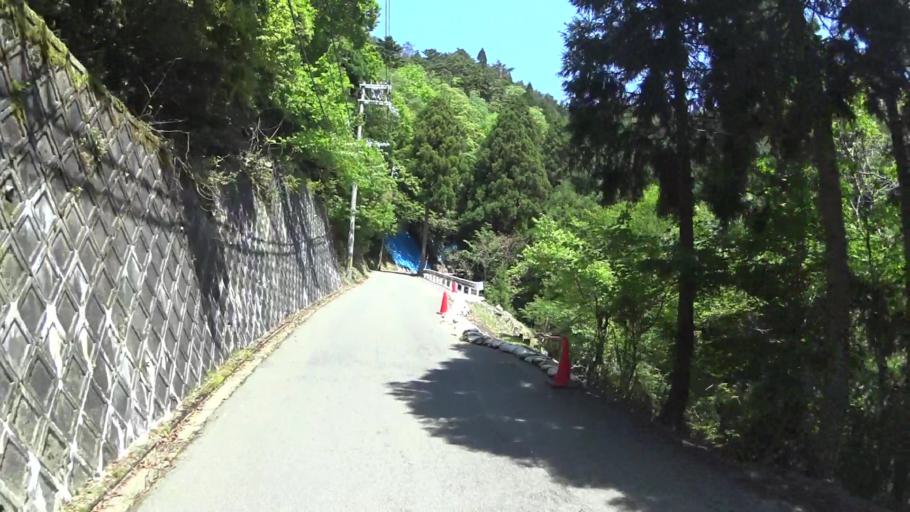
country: JP
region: Shiga Prefecture
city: Kitahama
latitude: 35.1564
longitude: 135.8078
